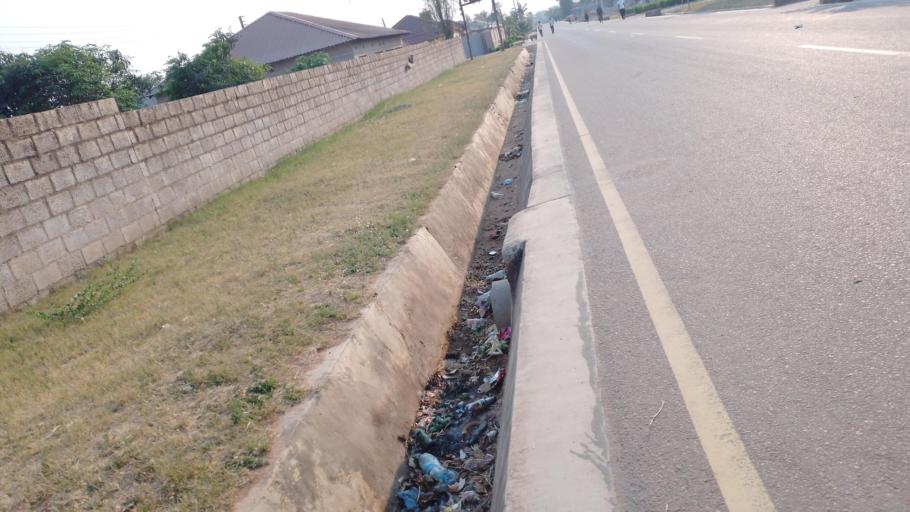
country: ZM
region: Lusaka
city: Lusaka
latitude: -15.3985
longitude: 28.3846
